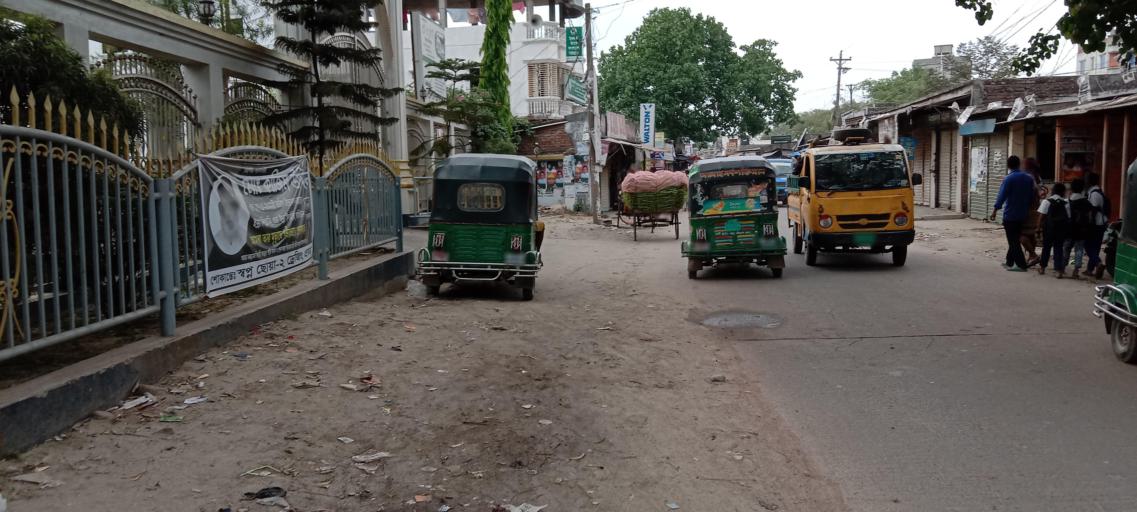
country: BD
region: Dhaka
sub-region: Dhaka
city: Dhaka
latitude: 23.6591
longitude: 90.4148
